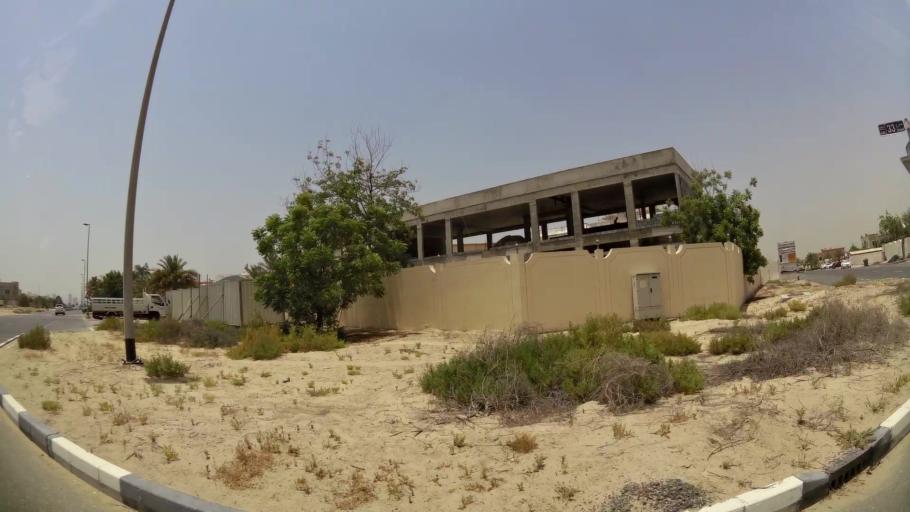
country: AE
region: Ash Shariqah
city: Sharjah
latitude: 25.1975
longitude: 55.3830
